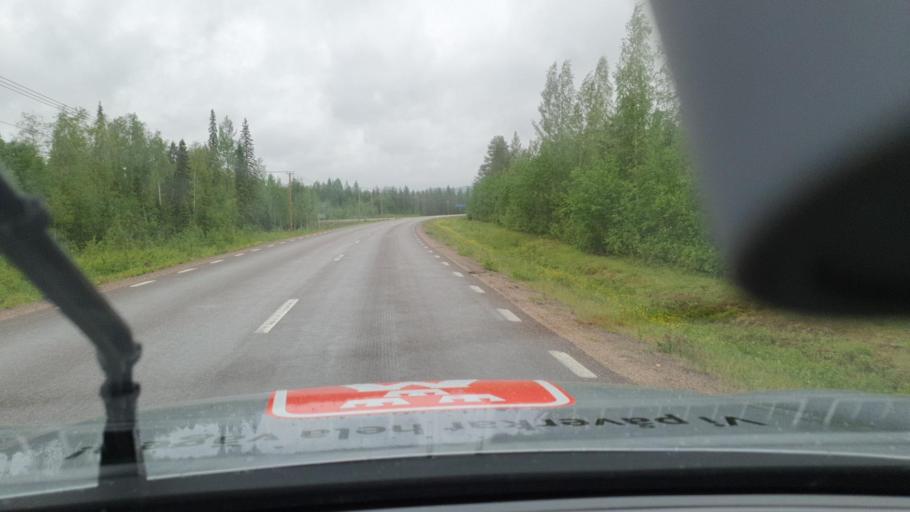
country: SE
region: Norrbotten
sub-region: Overkalix Kommun
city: OEverkalix
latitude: 66.4302
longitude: 22.9625
